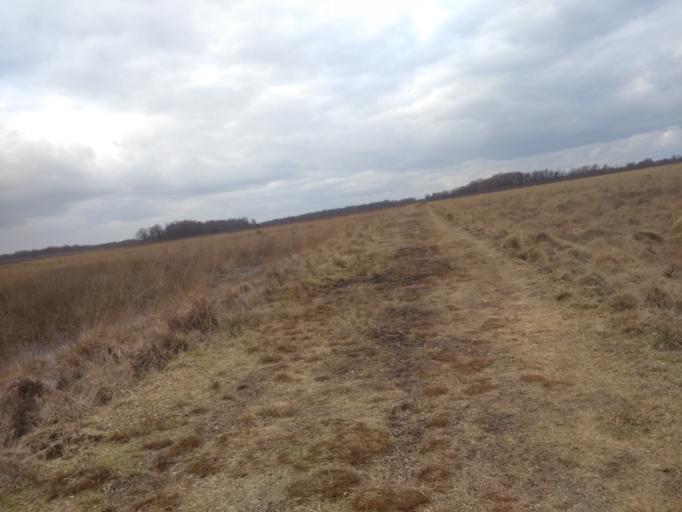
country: NL
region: Overijssel
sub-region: Gemeente Haaksbergen
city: Haaksbergen
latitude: 52.1222
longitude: 6.7876
